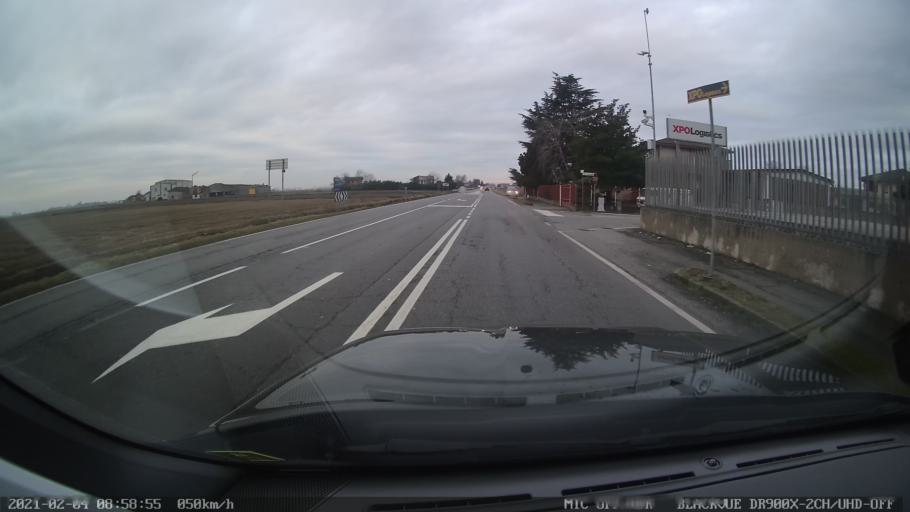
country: IT
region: Piedmont
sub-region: Provincia di Novara
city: San Pietro Mosezzo
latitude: 45.4537
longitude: 8.5577
